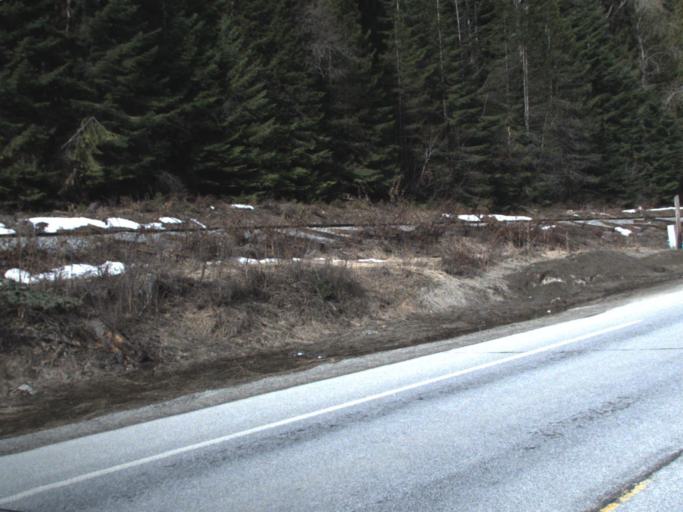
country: US
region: Washington
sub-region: Pend Oreille County
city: Newport
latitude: 48.2363
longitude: -117.2247
